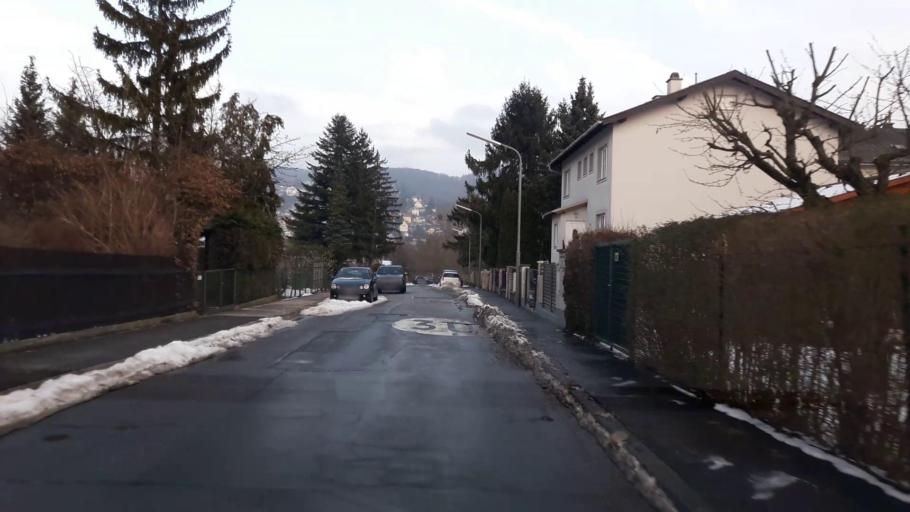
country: AT
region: Lower Austria
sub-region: Politischer Bezirk Wien-Umgebung
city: Purkersdorf
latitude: 48.2138
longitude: 16.2421
